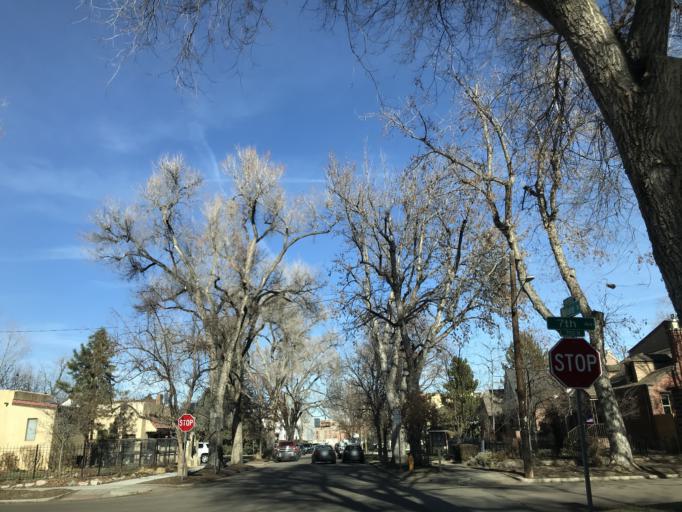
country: US
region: Colorado
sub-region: Arapahoe County
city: Glendale
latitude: 39.7272
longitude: -104.9371
